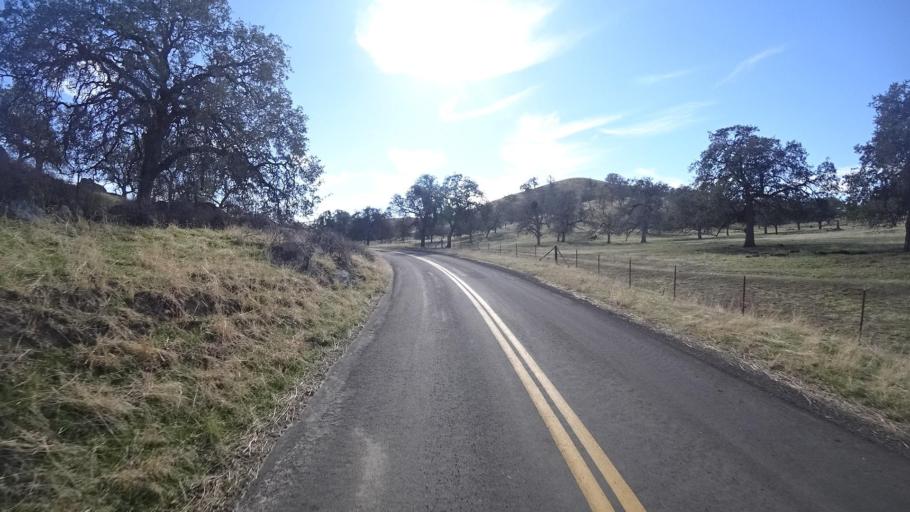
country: US
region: California
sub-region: Tulare County
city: Richgrove
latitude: 35.6693
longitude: -118.8496
